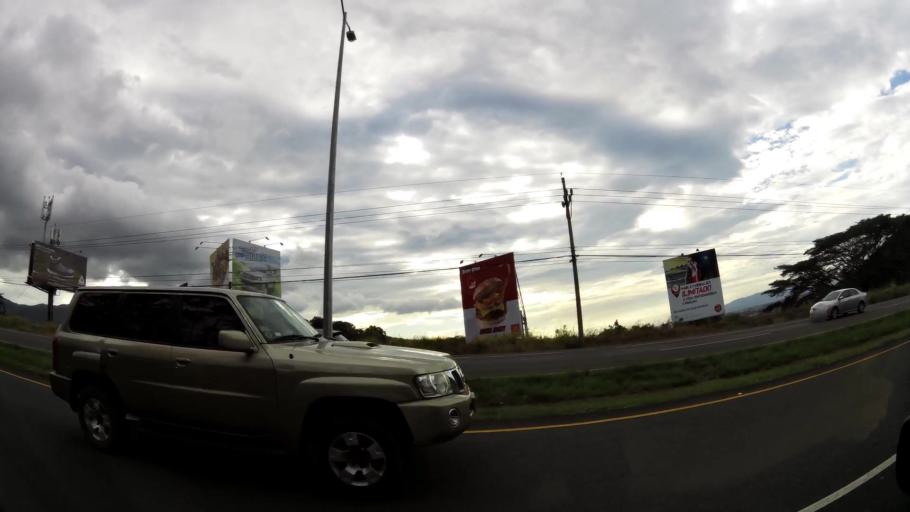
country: CR
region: San Jose
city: Santa Ana
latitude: 9.9456
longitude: -84.1734
